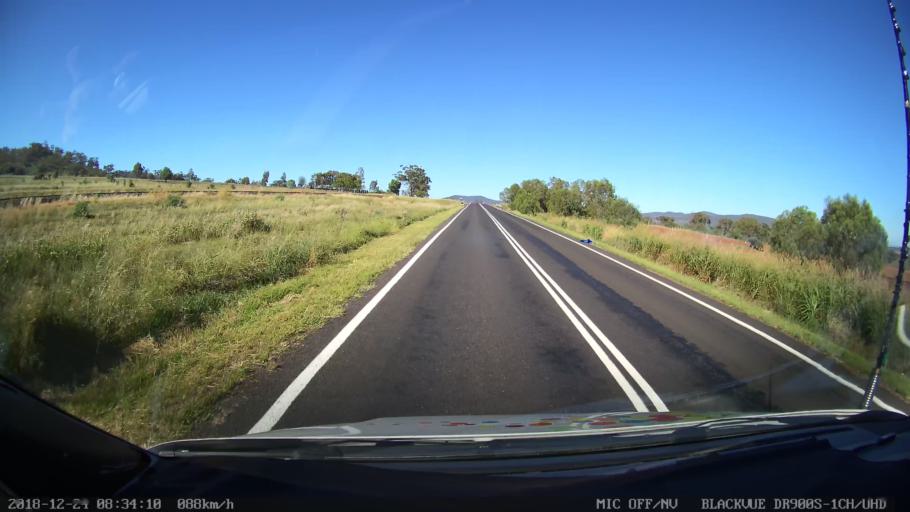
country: AU
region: New South Wales
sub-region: Liverpool Plains
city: Quirindi
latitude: -31.2909
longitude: 150.6742
